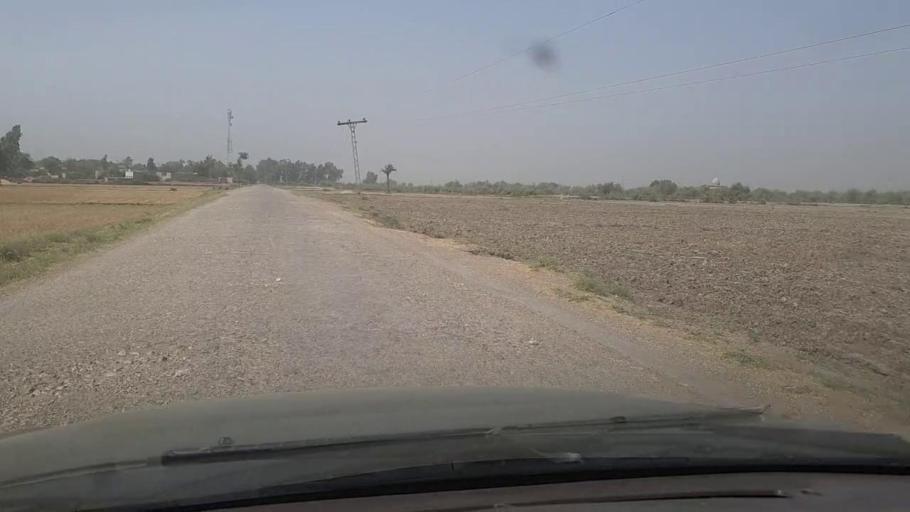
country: PK
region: Sindh
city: Garhi Yasin
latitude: 27.8647
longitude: 68.5524
